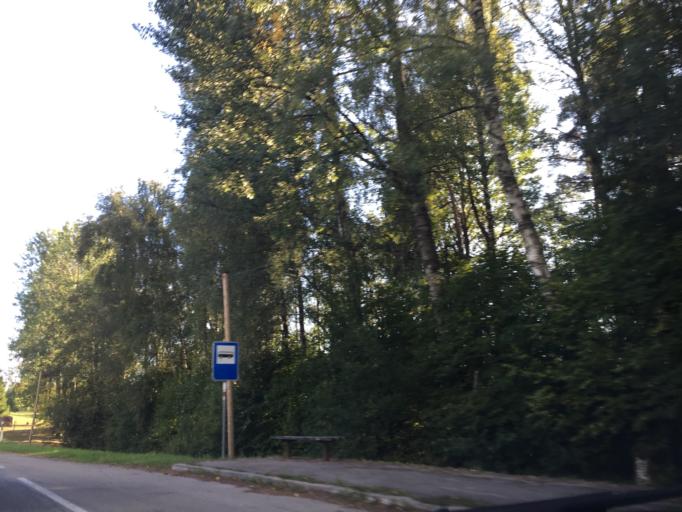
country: LV
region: Krimulda
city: Ragana
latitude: 57.1982
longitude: 24.7049
